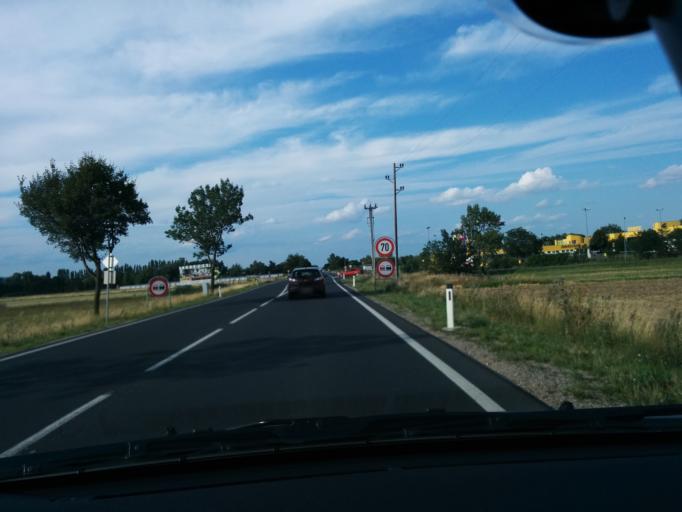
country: AT
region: Lower Austria
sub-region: Politischer Bezirk Baden
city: Teesdorf
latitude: 47.9597
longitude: 16.2706
